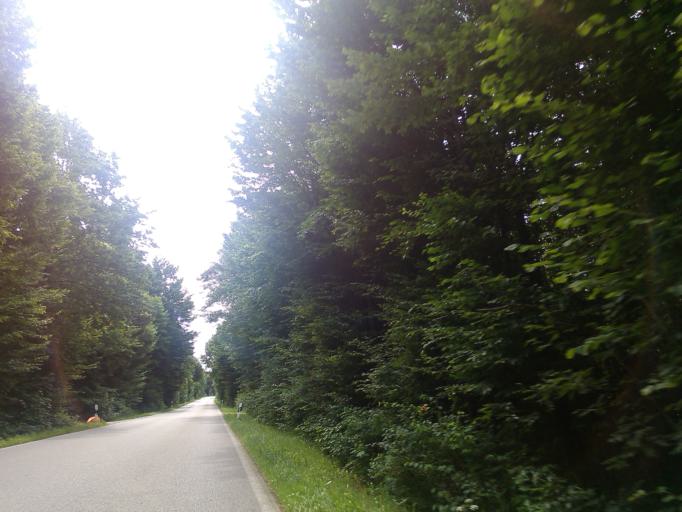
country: DE
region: Bavaria
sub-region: Upper Bavaria
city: Gauting
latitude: 48.0793
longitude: 11.3535
